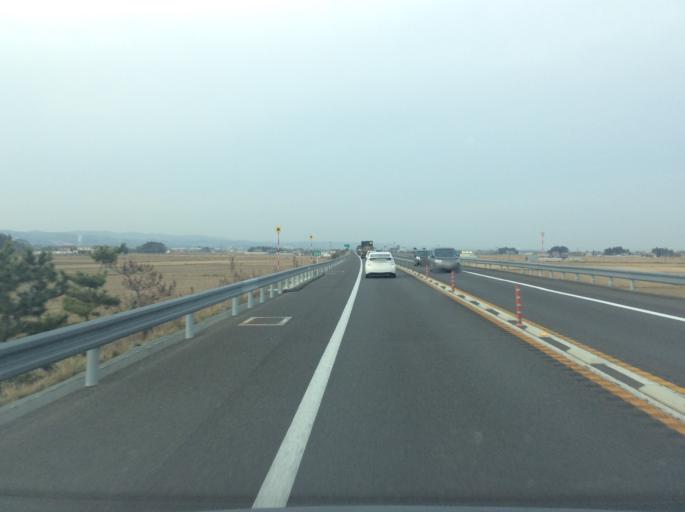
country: JP
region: Miyagi
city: Iwanuma
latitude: 38.0729
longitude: 140.8911
